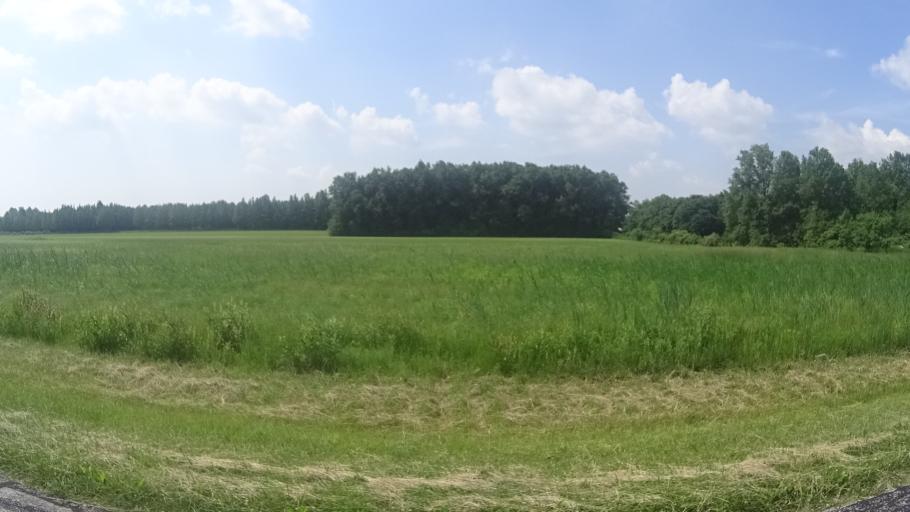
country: US
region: Ohio
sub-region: Erie County
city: Sandusky
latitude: 41.3601
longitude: -82.7043
